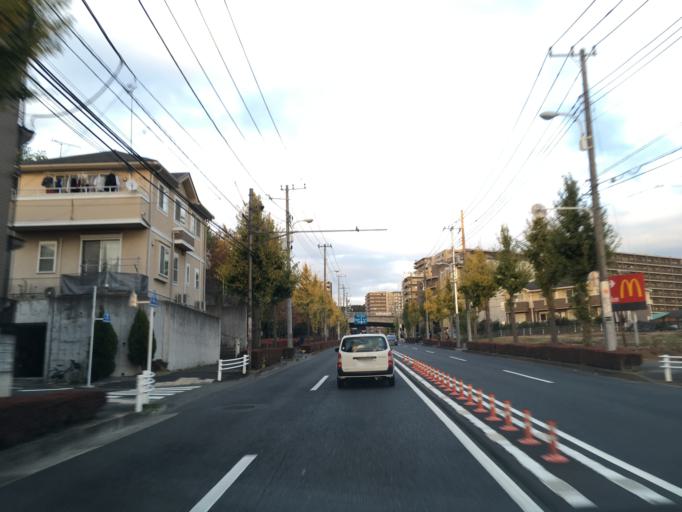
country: JP
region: Tokyo
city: Hachioji
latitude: 35.6008
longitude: 139.3638
